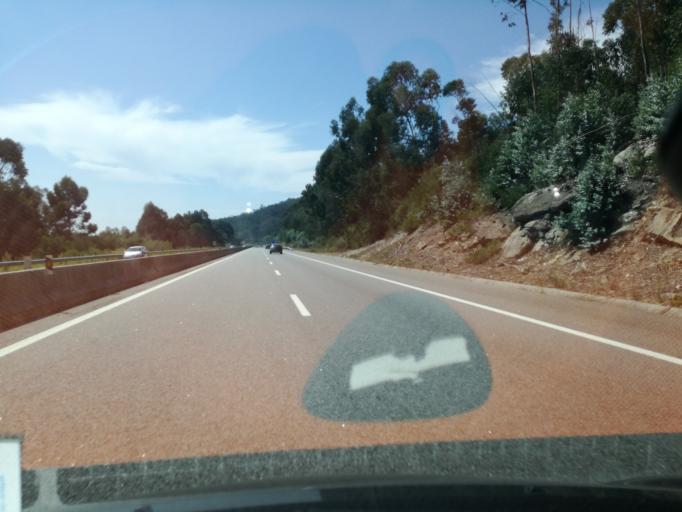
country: PT
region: Viana do Castelo
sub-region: Viana do Castelo
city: Meadela
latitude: 41.7560
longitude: -8.7962
